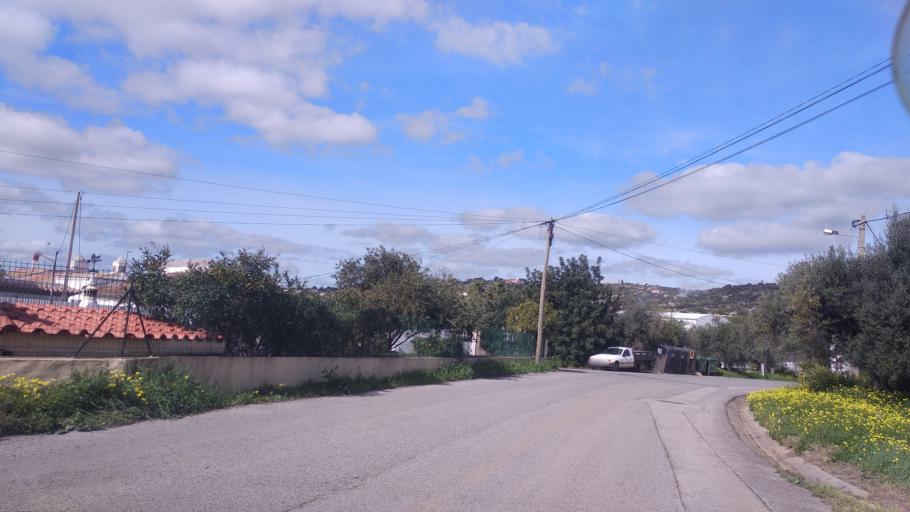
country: PT
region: Faro
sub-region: Sao Bras de Alportel
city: Sao Bras de Alportel
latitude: 37.1503
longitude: -7.9170
